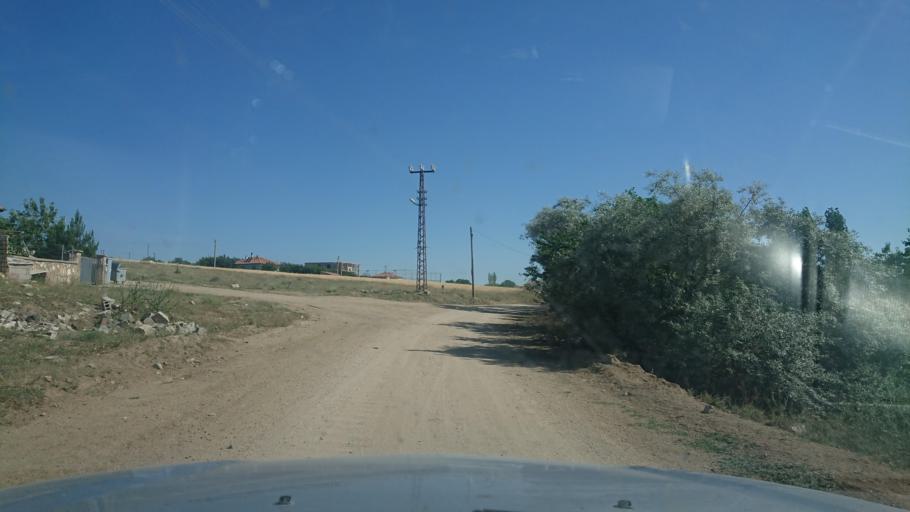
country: TR
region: Aksaray
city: Agacoren
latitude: 38.8639
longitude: 33.9128
